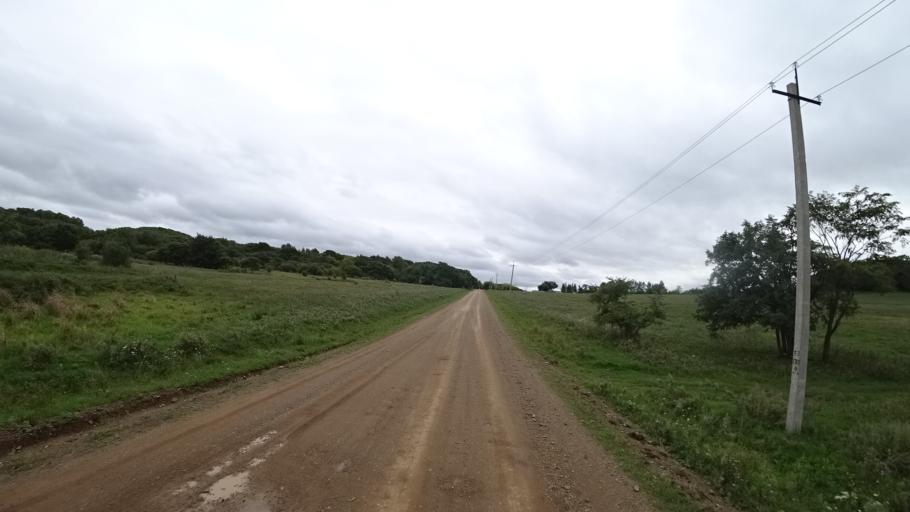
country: RU
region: Primorskiy
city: Chernigovka
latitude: 44.4657
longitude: 132.5879
